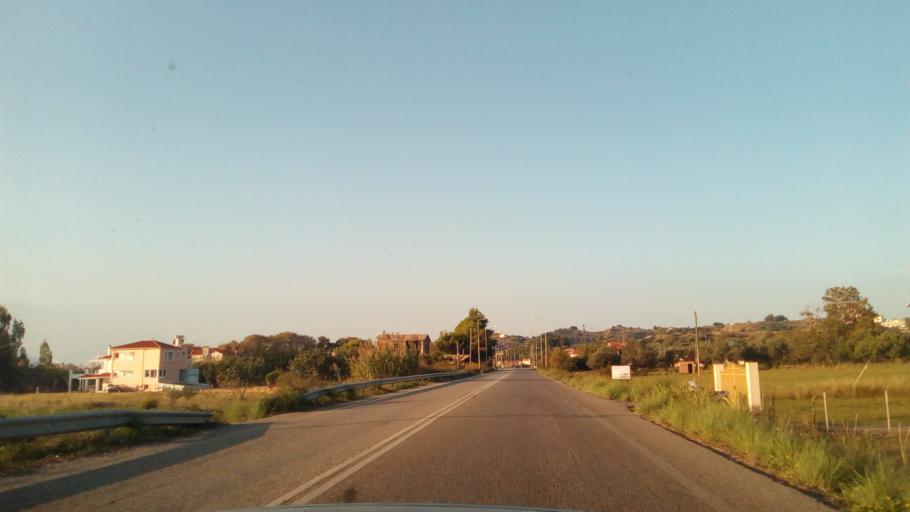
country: GR
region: West Greece
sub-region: Nomos Aitolias kai Akarnanias
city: Nafpaktos
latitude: 38.3730
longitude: 21.7846
